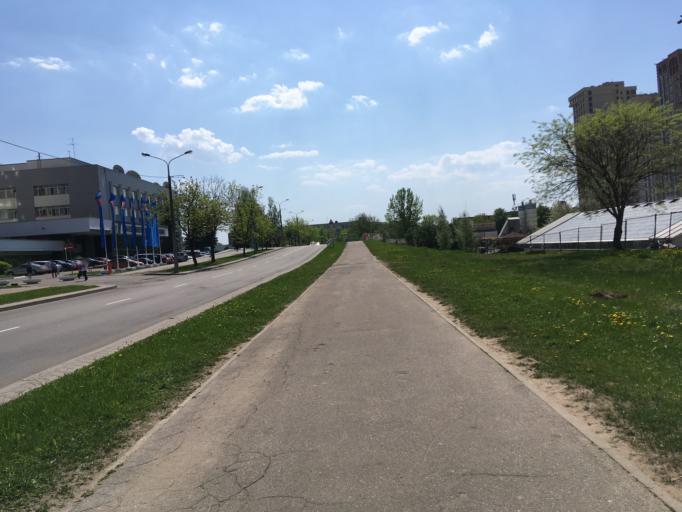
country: BY
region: Minsk
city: Minsk
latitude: 53.9244
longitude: 27.6280
